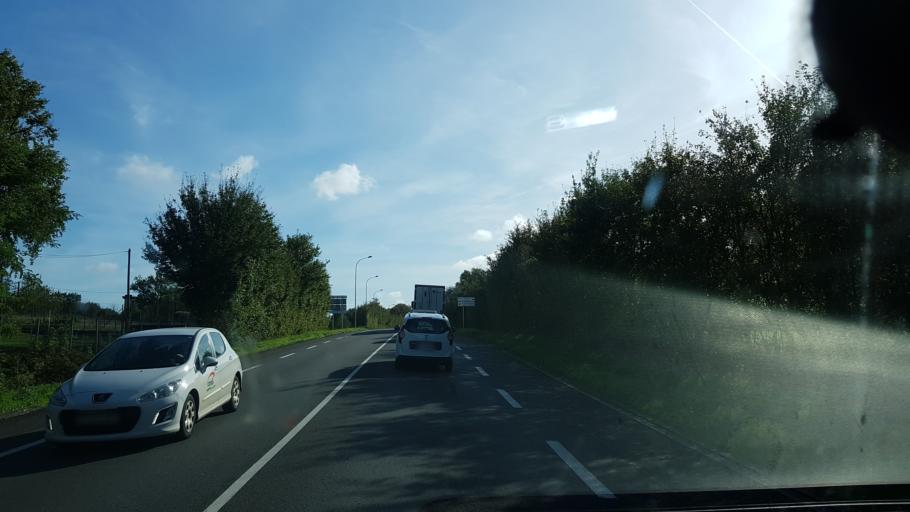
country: FR
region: Poitou-Charentes
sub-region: Departement de la Charente
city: Saint-Claud
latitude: 45.8842
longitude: 0.4694
